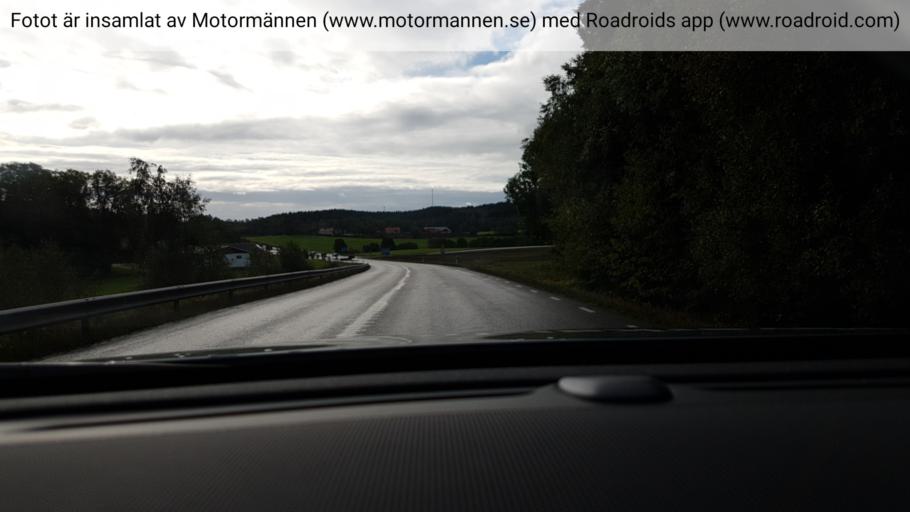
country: SE
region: Vaestra Goetaland
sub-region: Harryda Kommun
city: Ravlanda
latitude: 57.5573
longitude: 12.5189
